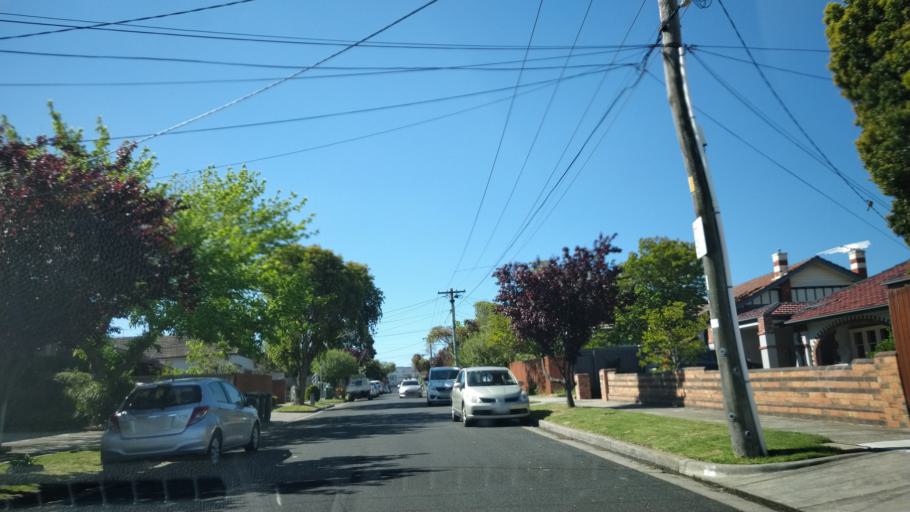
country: AU
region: Victoria
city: Ormond
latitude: -37.9065
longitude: 145.0427
